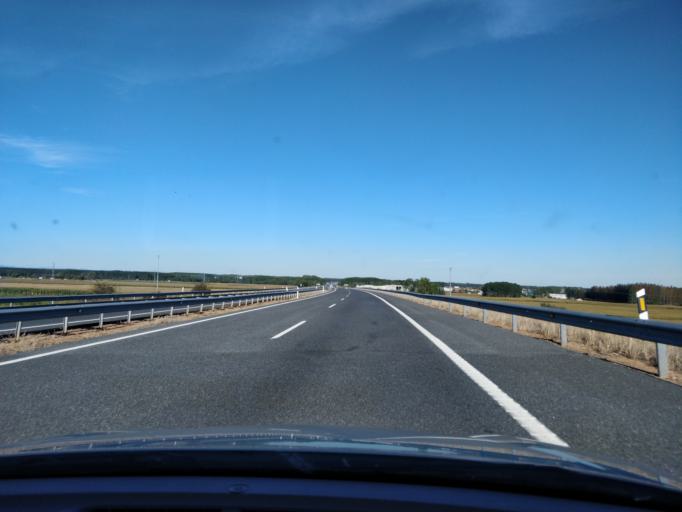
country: ES
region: Castille and Leon
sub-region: Provincia de Leon
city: Villarejo de Orbigo
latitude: 42.4454
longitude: -5.9331
